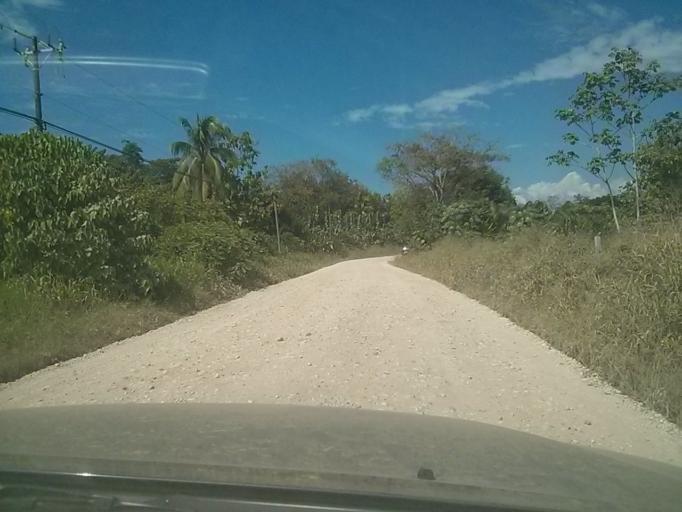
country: CR
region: Puntarenas
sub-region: Canton de Golfito
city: Golfito
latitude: 8.4544
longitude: -83.0489
